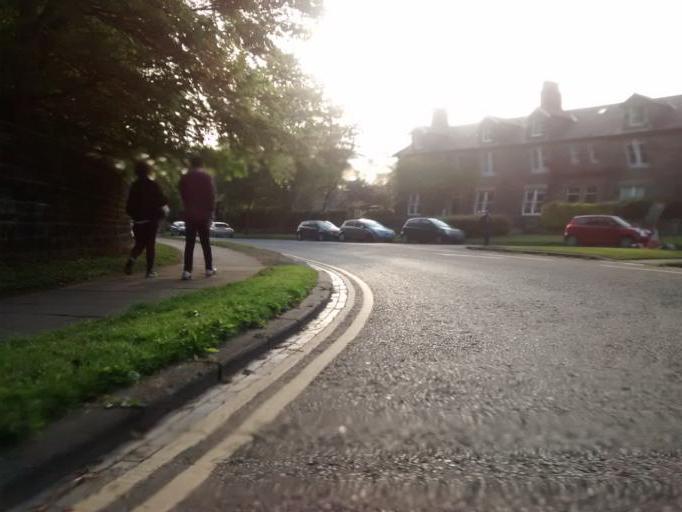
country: GB
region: England
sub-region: County Durham
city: Durham
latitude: 54.7690
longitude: -1.5685
